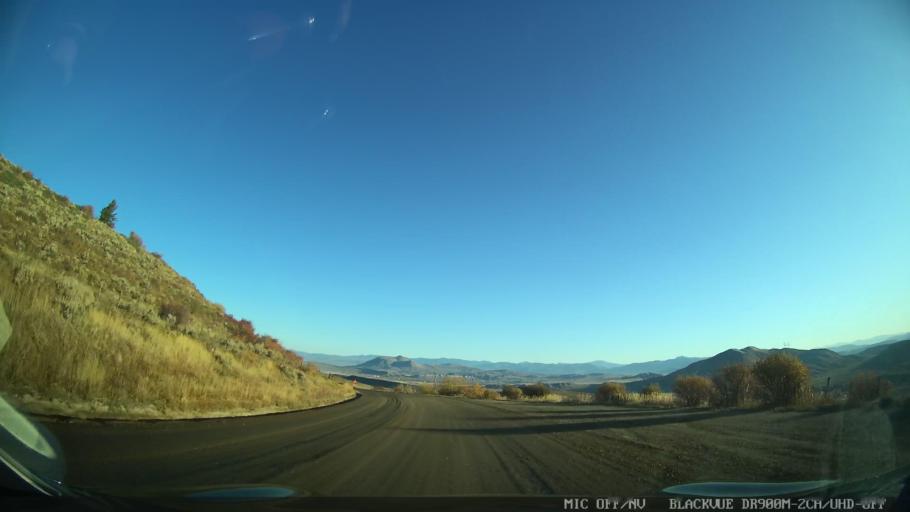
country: US
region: Colorado
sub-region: Grand County
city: Kremmling
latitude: 39.9985
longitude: -106.4072
